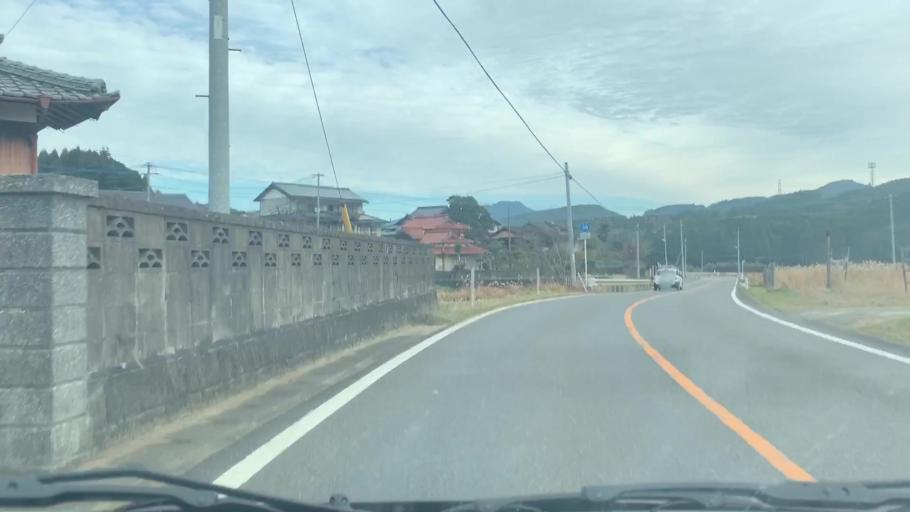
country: JP
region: Saga Prefecture
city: Takeocho-takeo
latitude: 33.2185
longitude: 129.9630
